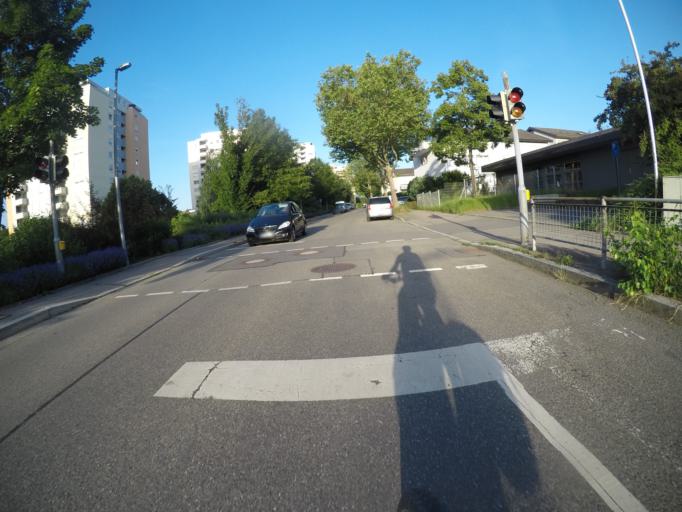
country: DE
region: Baden-Wuerttemberg
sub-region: Regierungsbezirk Stuttgart
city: Boeblingen
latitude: 48.6764
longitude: 9.0261
